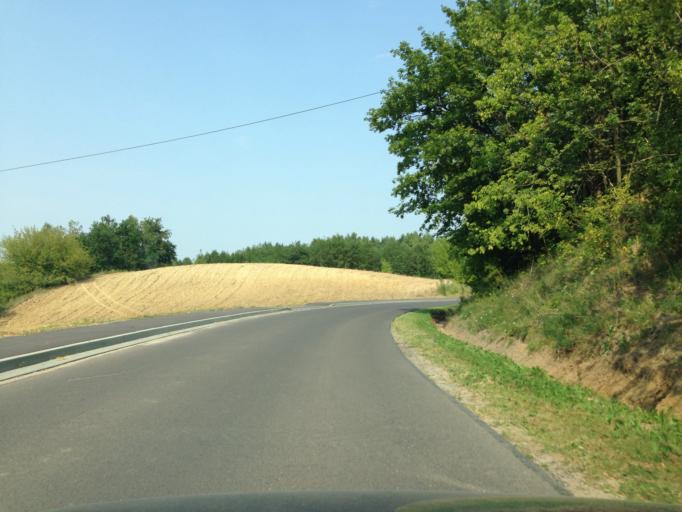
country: PL
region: Kujawsko-Pomorskie
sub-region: Powiat golubsko-dobrzynski
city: Golub-Dobrzyn
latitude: 53.0696
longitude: 19.0317
